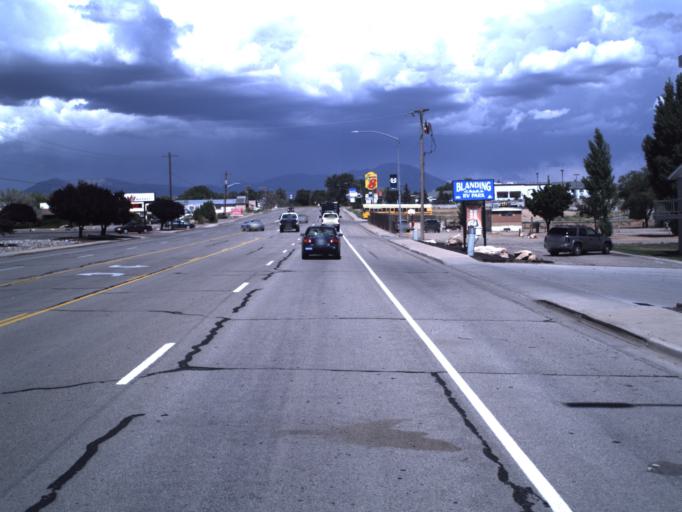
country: US
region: Utah
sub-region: San Juan County
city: Blanding
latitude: 37.6121
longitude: -109.4789
